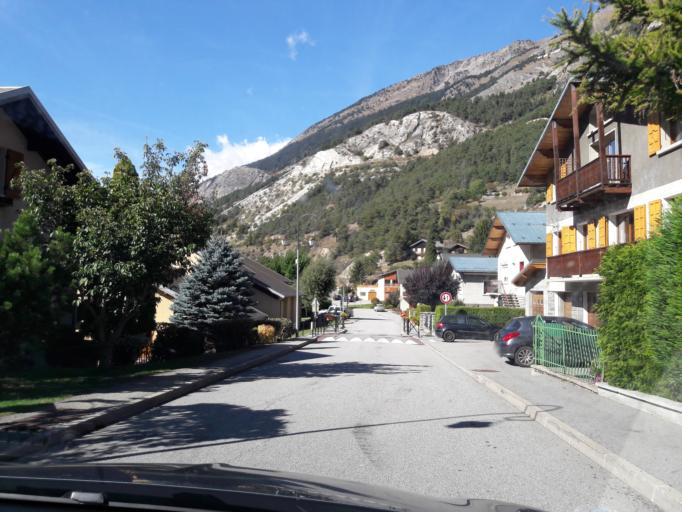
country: FR
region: Rhone-Alpes
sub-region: Departement de la Savoie
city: Modane
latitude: 45.2155
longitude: 6.7213
